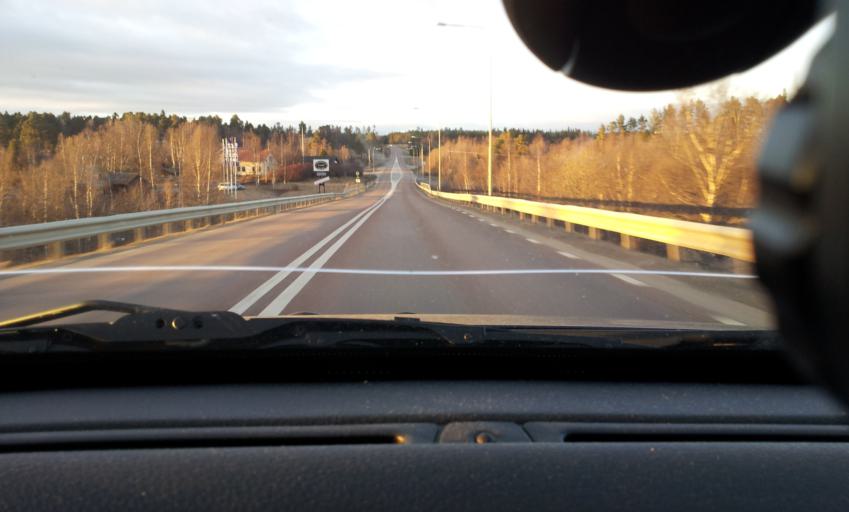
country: SE
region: Jaemtland
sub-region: Bergs Kommun
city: Hoverberg
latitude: 62.9126
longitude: 14.5254
